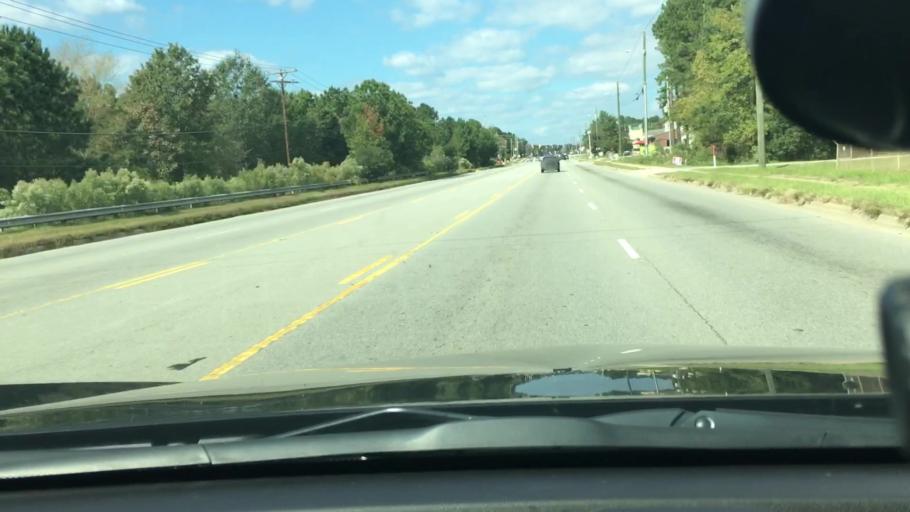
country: US
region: North Carolina
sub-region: Wake County
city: Apex
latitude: 35.7090
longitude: -78.8372
